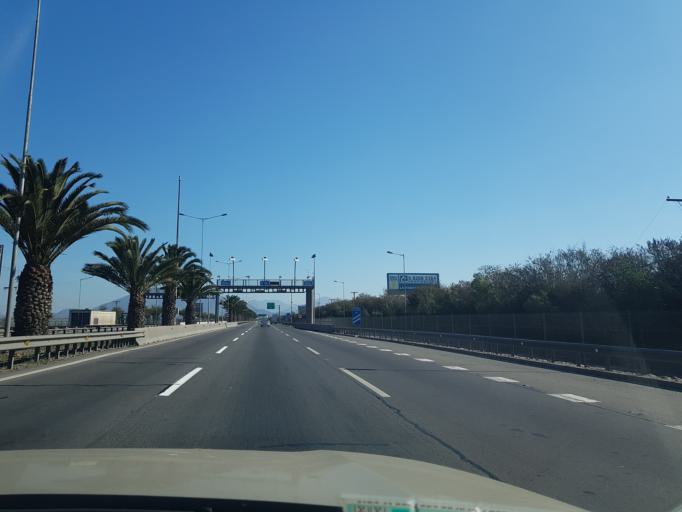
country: CL
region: Santiago Metropolitan
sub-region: Provincia de Santiago
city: Lo Prado
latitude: -33.3987
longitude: -70.7747
